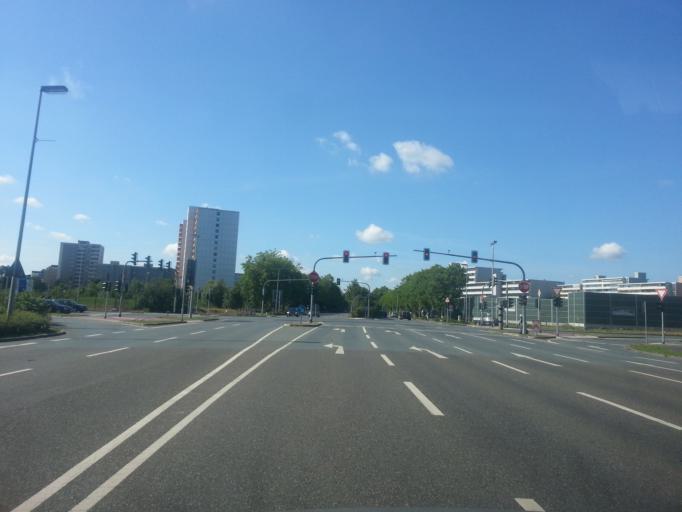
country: DE
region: Hesse
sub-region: Regierungsbezirk Darmstadt
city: Dietzenbach
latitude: 50.0185
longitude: 8.7809
